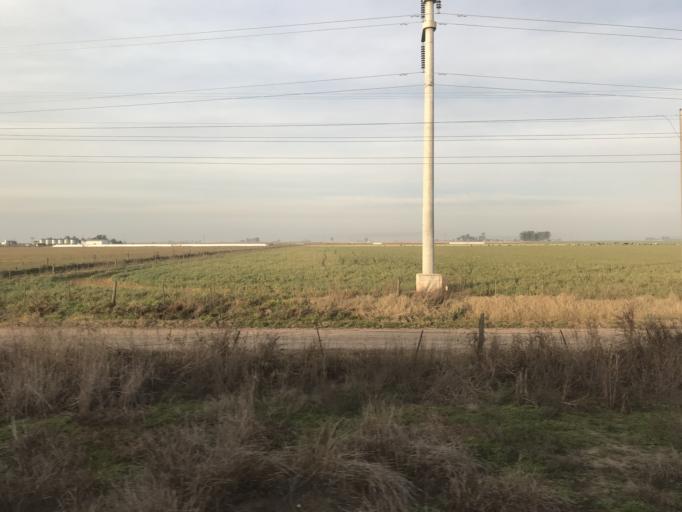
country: AR
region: Cordoba
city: Marcos Juarez
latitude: -32.6821
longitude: -62.2013
